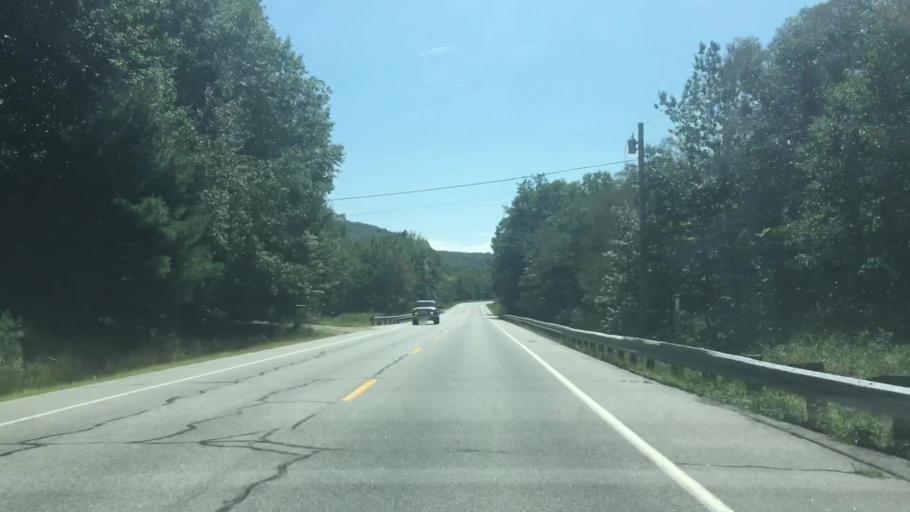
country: US
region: Maine
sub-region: Androscoggin County
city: Sabattus
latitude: 44.1529
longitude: -70.0358
